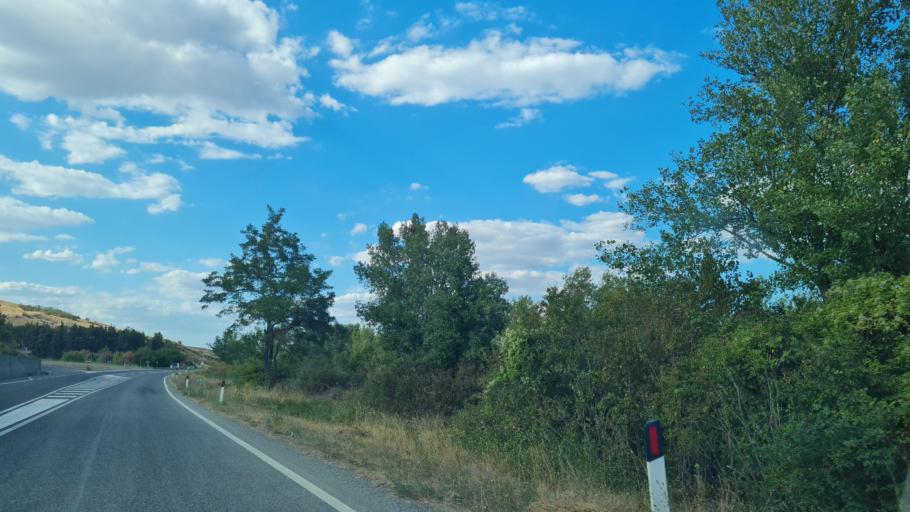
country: IT
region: Tuscany
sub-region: Provincia di Siena
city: Abbadia San Salvatore
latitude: 42.9481
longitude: 11.7087
